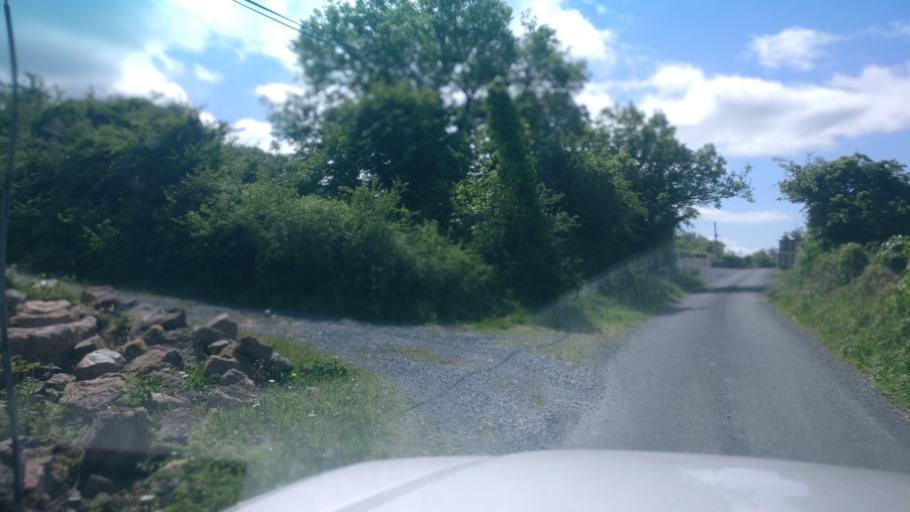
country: IE
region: Connaught
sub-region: County Galway
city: Gort
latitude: 53.1290
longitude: -8.7064
